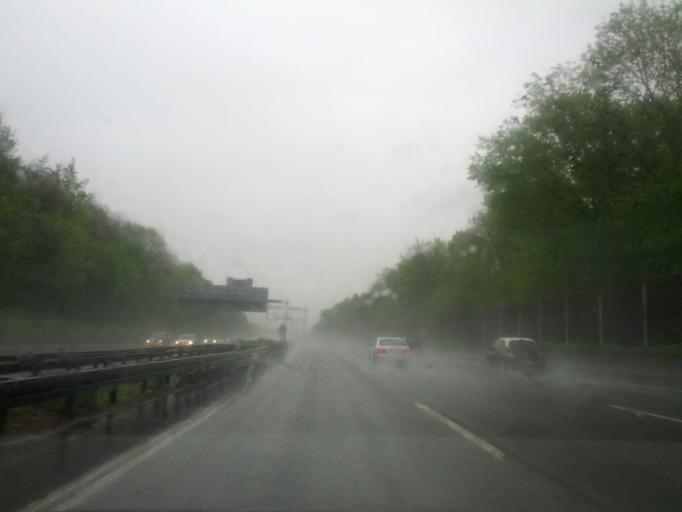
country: DE
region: North Rhine-Westphalia
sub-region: Regierungsbezirk Koln
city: Poll
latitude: 50.8916
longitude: 6.9814
